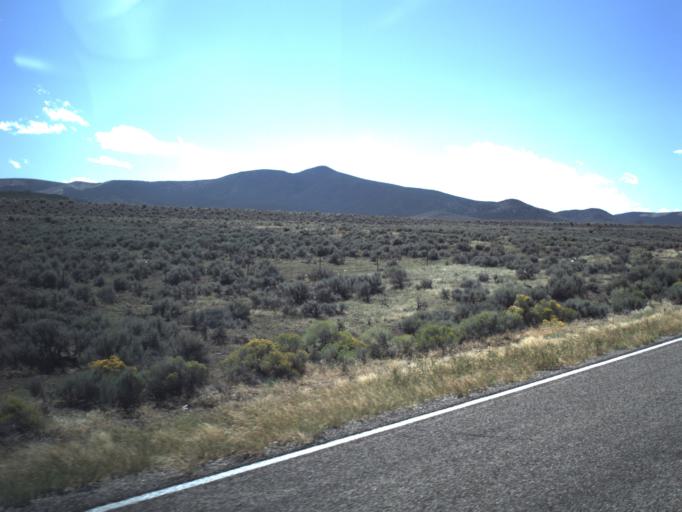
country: US
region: Utah
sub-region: Beaver County
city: Milford
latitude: 38.2010
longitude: -112.9313
